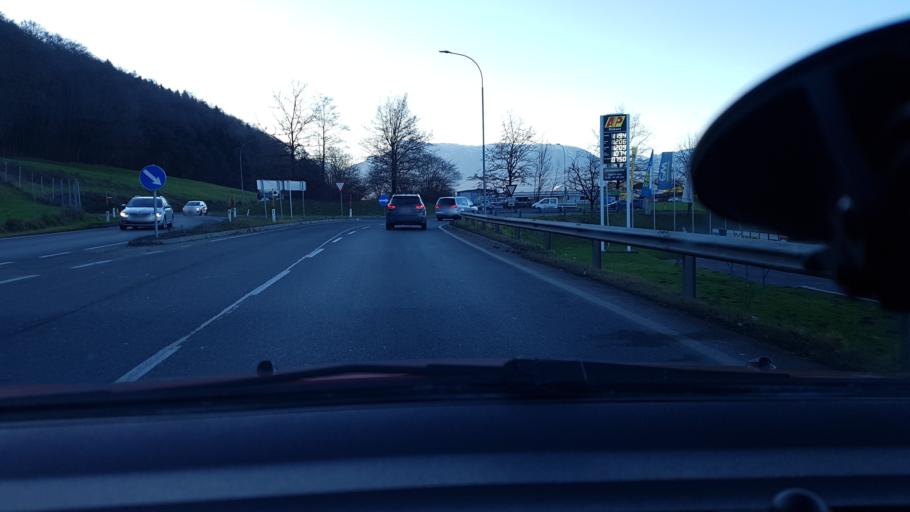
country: AT
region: Salzburg
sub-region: Politischer Bezirk Salzburg-Umgebung
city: Anthering
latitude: 47.8647
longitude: 13.0169
